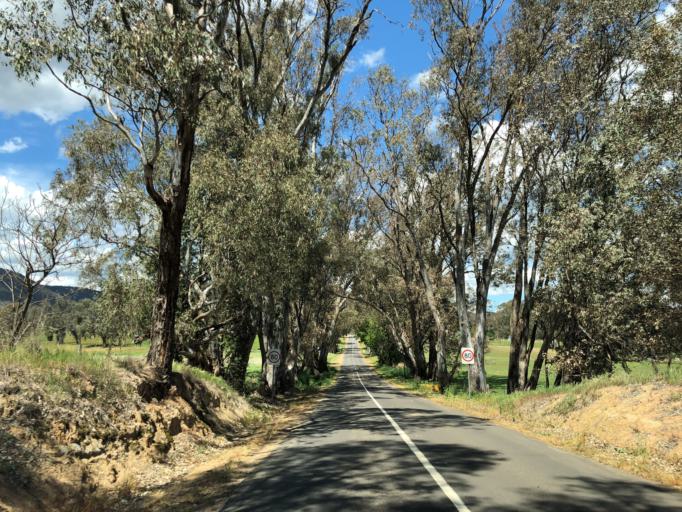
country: AU
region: Victoria
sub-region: Benalla
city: Benalla
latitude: -36.7337
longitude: 146.1110
